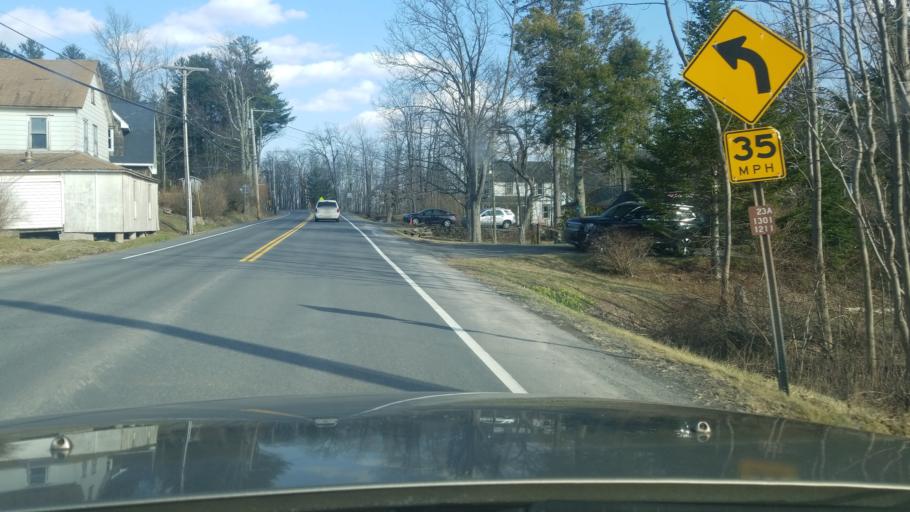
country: US
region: New York
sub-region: Ulster County
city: Manorville
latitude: 42.1958
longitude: -74.1049
